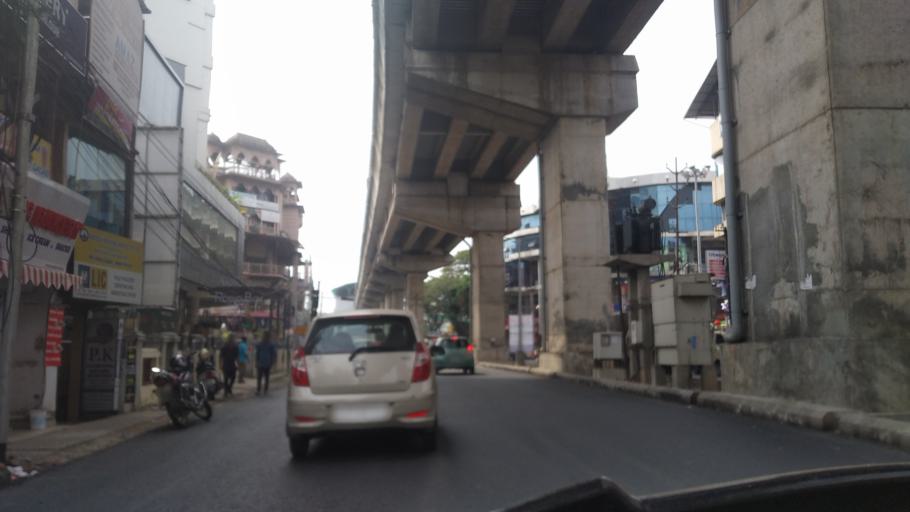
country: IN
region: Kerala
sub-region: Ernakulam
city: Cochin
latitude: 9.9675
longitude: 76.3005
